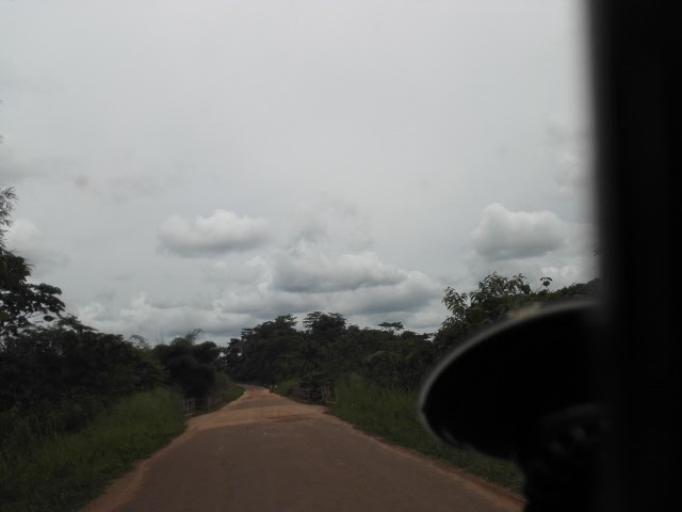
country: CD
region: Eastern Province
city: Kisangani
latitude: 0.4625
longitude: 25.3507
